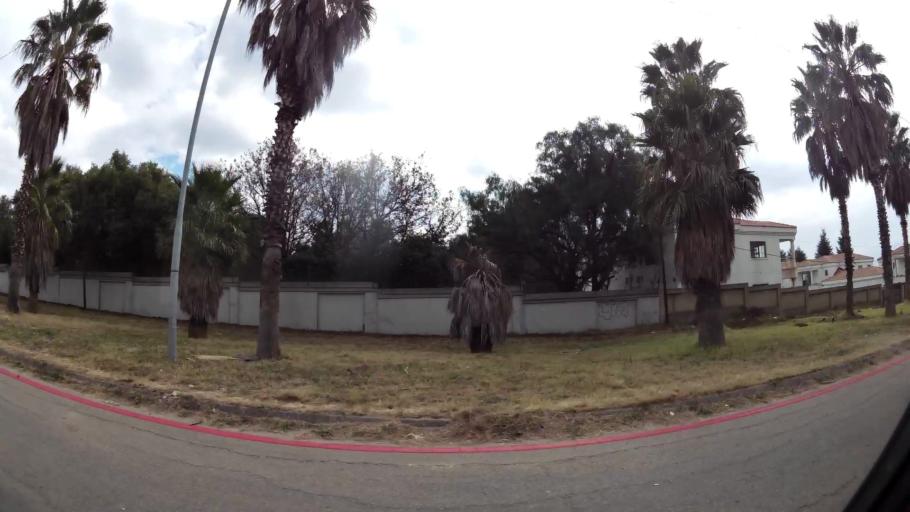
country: ZA
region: Gauteng
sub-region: West Rand District Municipality
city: Muldersdriseloop
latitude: -26.0770
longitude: 27.8611
